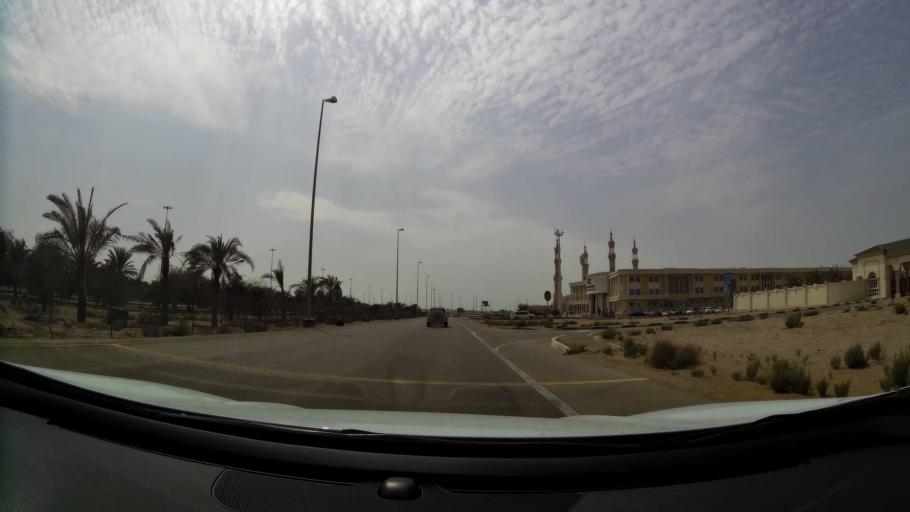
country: AE
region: Abu Dhabi
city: Abu Dhabi
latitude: 24.5174
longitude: 54.6678
